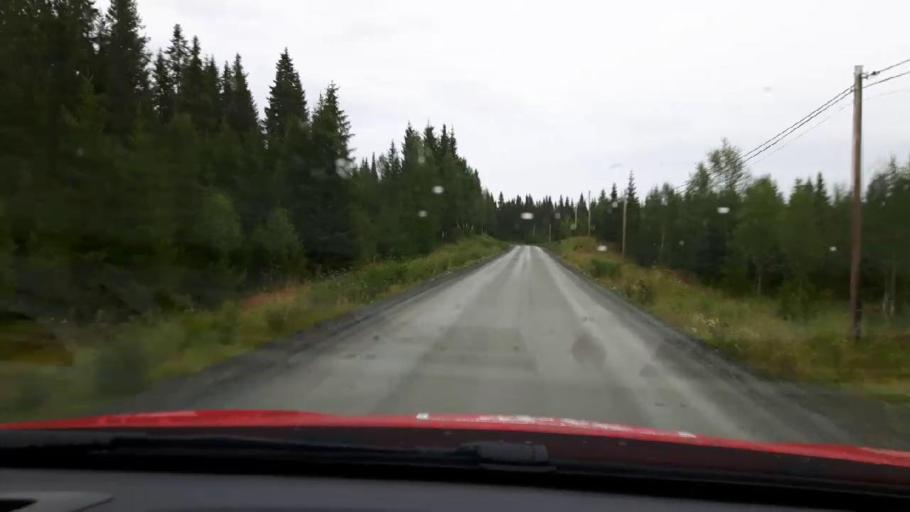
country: SE
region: Jaemtland
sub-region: Are Kommun
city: Are
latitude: 63.4817
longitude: 12.7955
